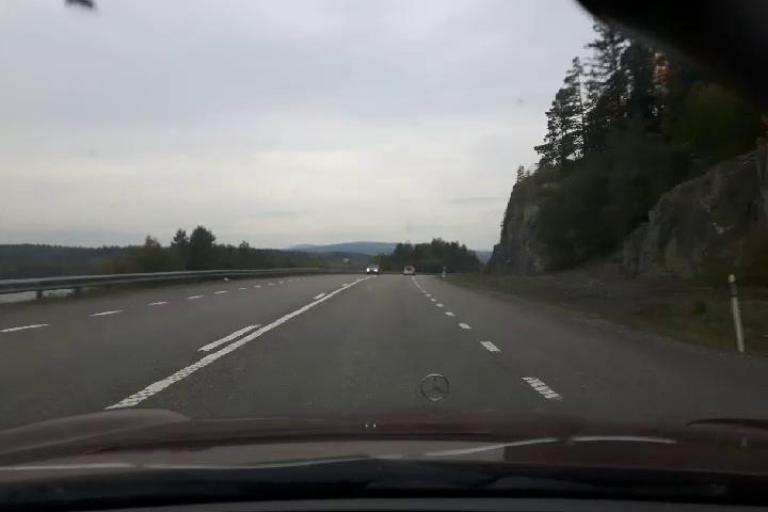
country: SE
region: Vaesternorrland
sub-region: Kramfors Kommun
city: Nordingra
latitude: 63.0078
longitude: 18.2268
